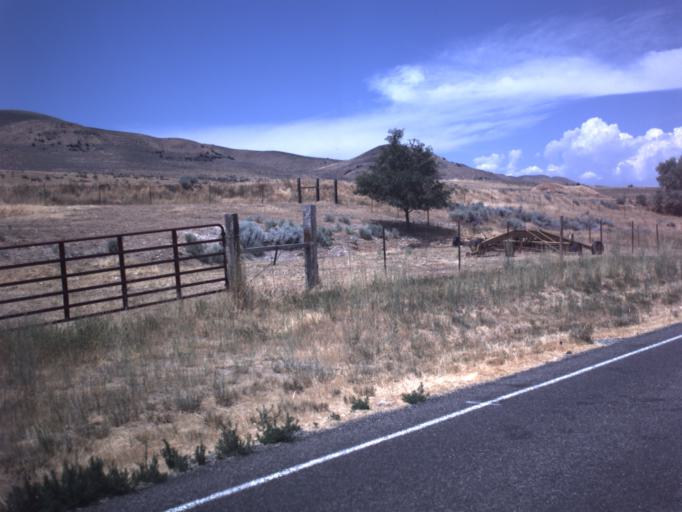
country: US
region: Utah
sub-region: Box Elder County
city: Tremonton
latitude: 41.6620
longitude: -112.2963
